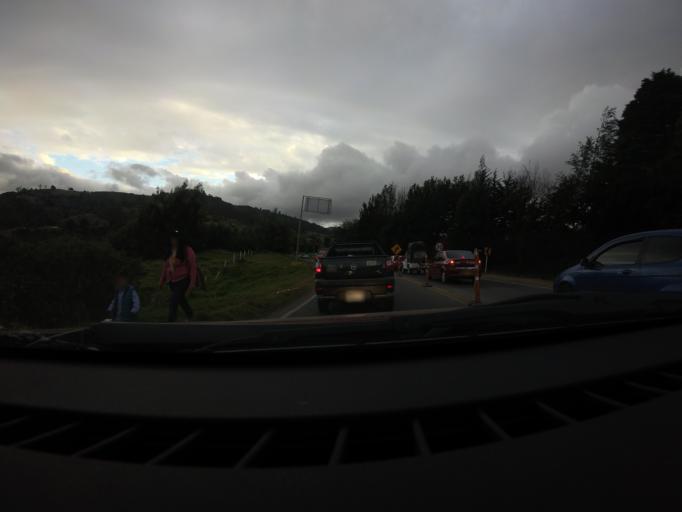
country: CO
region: Boyaca
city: Samaca
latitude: 5.4531
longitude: -73.4275
